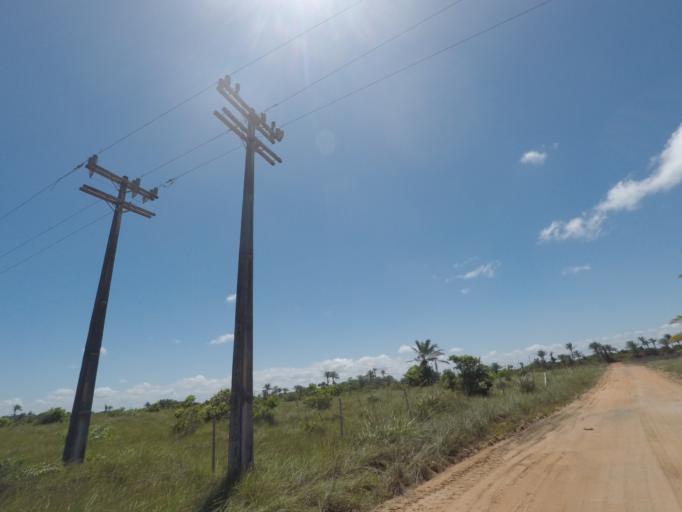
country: BR
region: Bahia
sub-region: Marau
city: Marau
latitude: -13.9677
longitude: -38.9447
